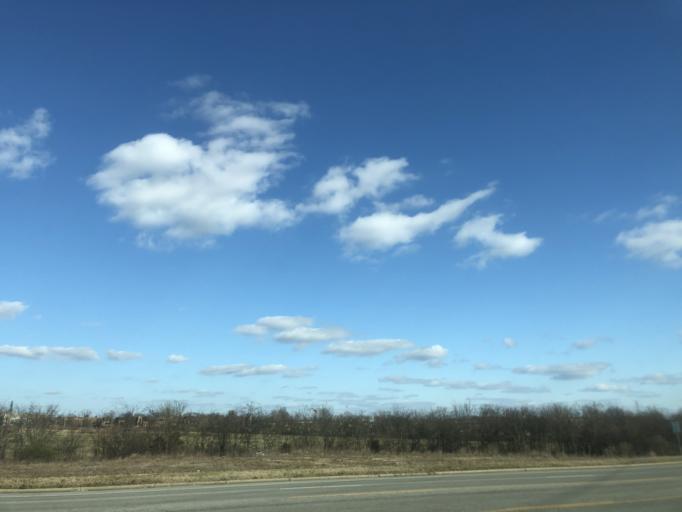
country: US
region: Tennessee
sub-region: Sumner County
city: Gallatin
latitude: 36.3592
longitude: -86.5044
